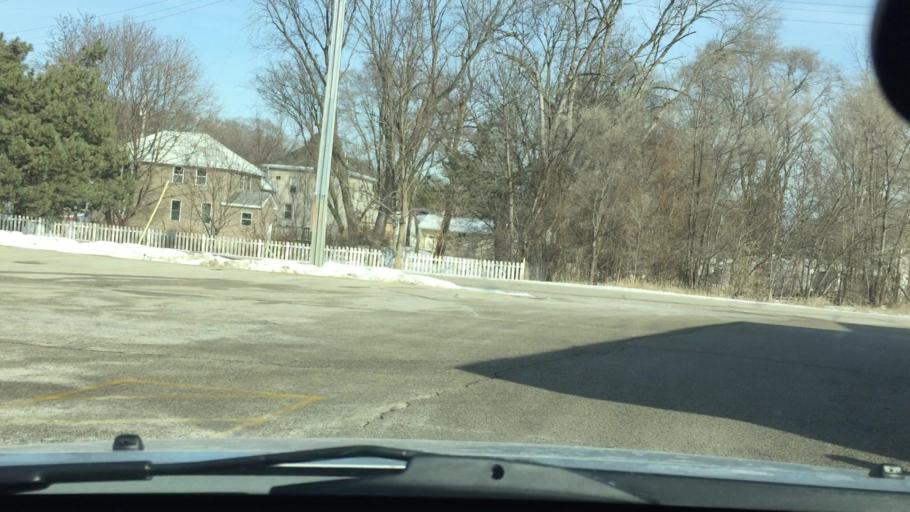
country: US
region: Wisconsin
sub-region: Waukesha County
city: Eagle
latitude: 42.8802
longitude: -88.4734
